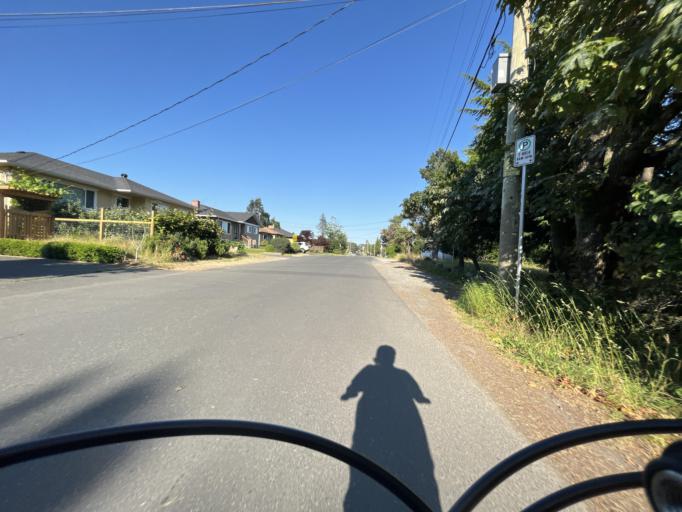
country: CA
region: British Columbia
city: Oak Bay
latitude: 48.4378
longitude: -123.3262
